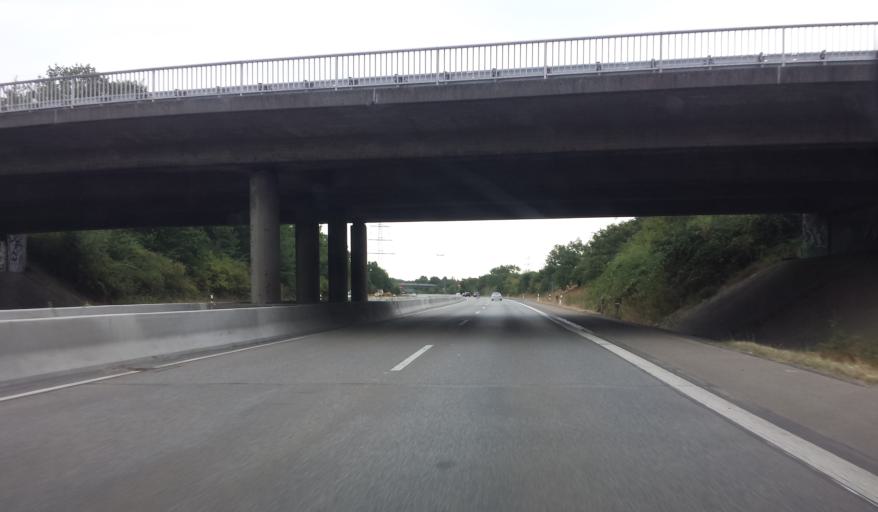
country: DE
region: Hesse
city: Kelsterbach
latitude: 50.0622
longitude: 8.5495
